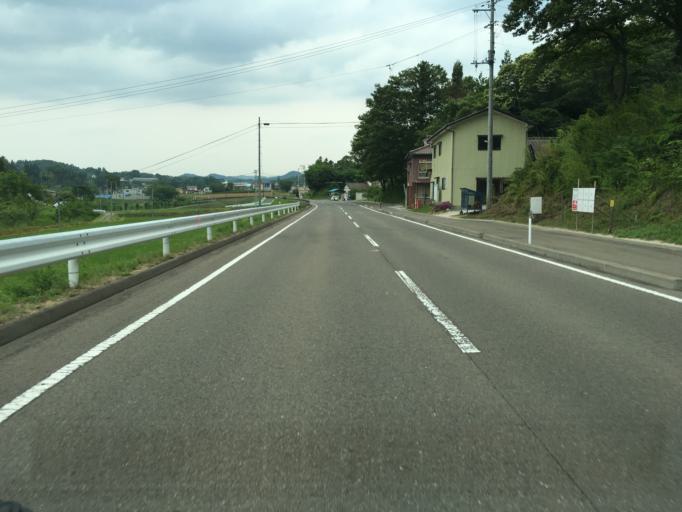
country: JP
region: Fukushima
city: Nihommatsu
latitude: 37.6472
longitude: 140.5350
